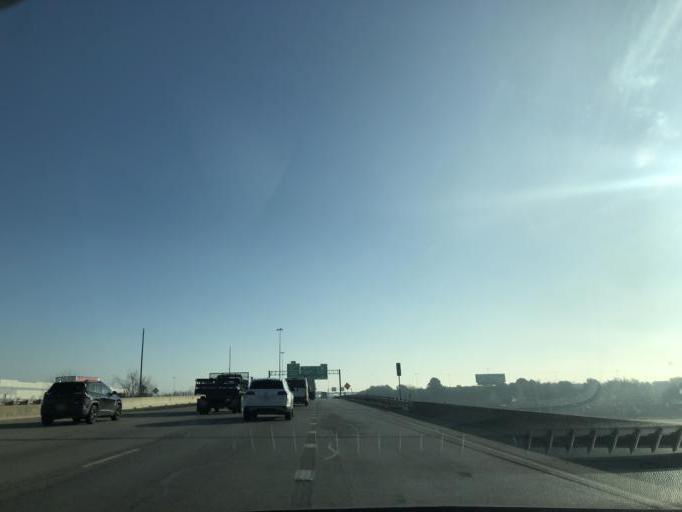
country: US
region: Texas
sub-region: Tarrant County
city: Blue Mound
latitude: 32.8386
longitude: -97.3224
